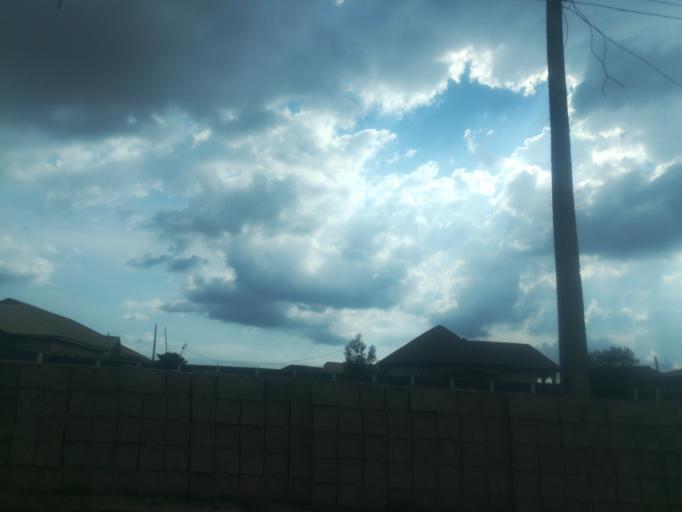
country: NG
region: Oyo
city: Ibadan
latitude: 7.4031
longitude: 3.8339
